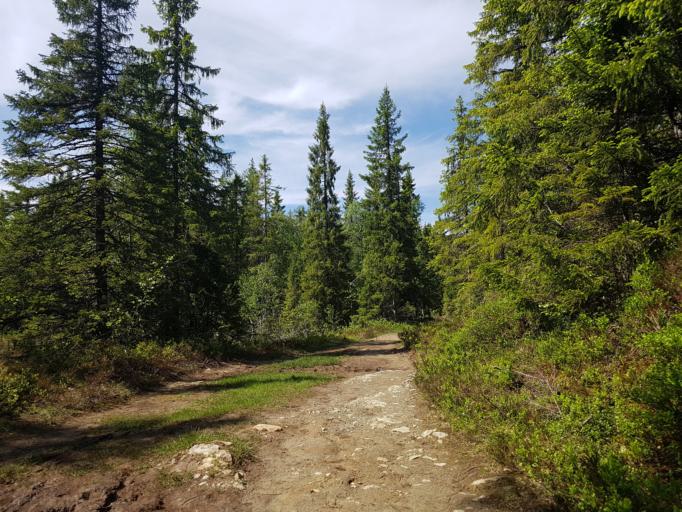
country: NO
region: Sor-Trondelag
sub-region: Trondheim
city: Trondheim
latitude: 63.4169
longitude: 10.3018
